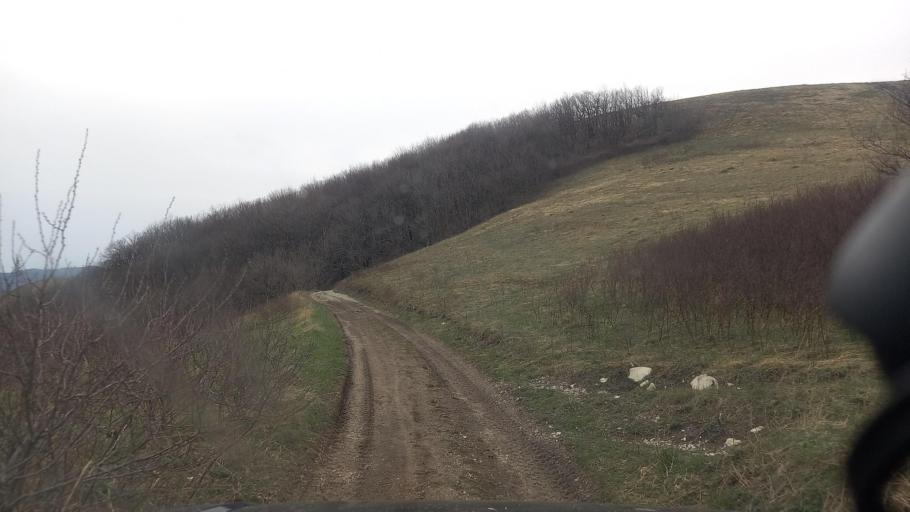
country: RU
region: Krasnodarskiy
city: Divnomorskoye
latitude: 44.6158
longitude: 38.2170
